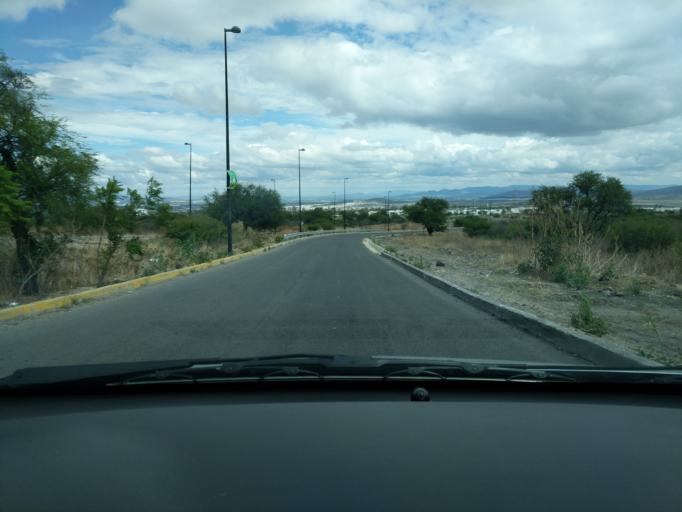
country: MX
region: Queretaro
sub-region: El Marques
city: La Pradera
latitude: 20.6687
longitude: -100.3169
